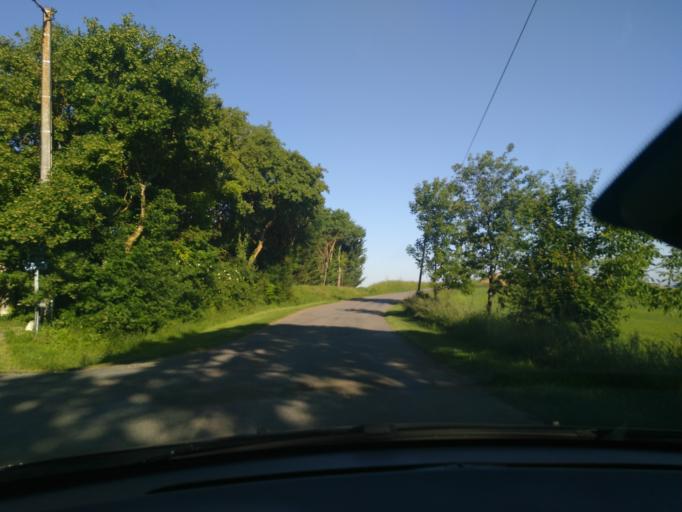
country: FR
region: Midi-Pyrenees
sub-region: Departement du Tarn-et-Garonne
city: Beaumont-de-Lomagne
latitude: 43.7824
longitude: 0.9747
